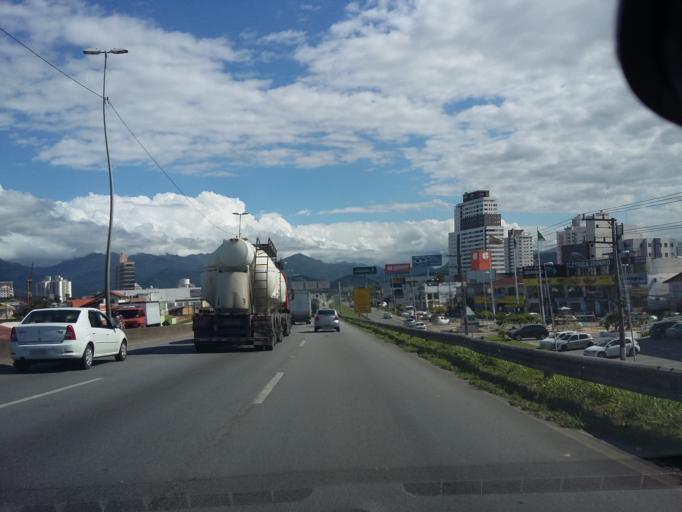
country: BR
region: Santa Catarina
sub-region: Palhoca
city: Palhoca
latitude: -27.6400
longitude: -48.6673
